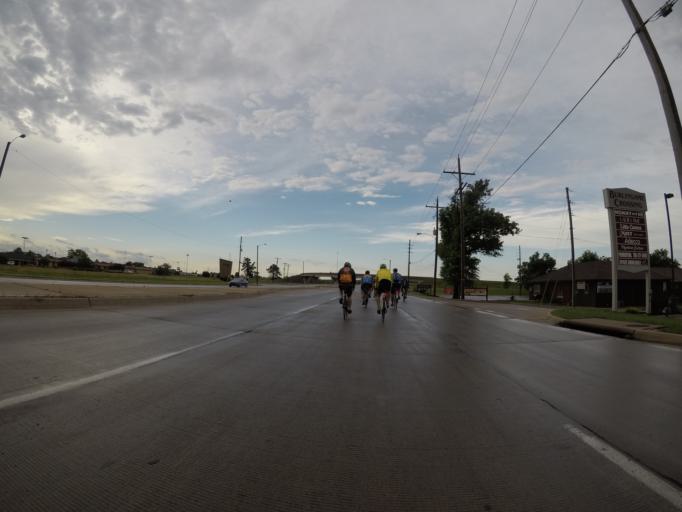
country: US
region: Kansas
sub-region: Shawnee County
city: Topeka
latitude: 39.0002
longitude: -95.7060
